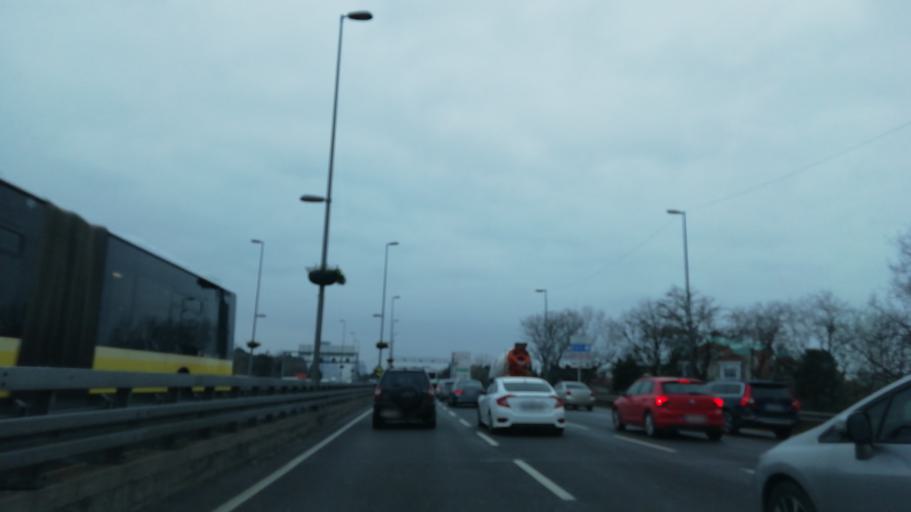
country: TR
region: Istanbul
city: UEskuedar
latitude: 41.0203
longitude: 29.0496
